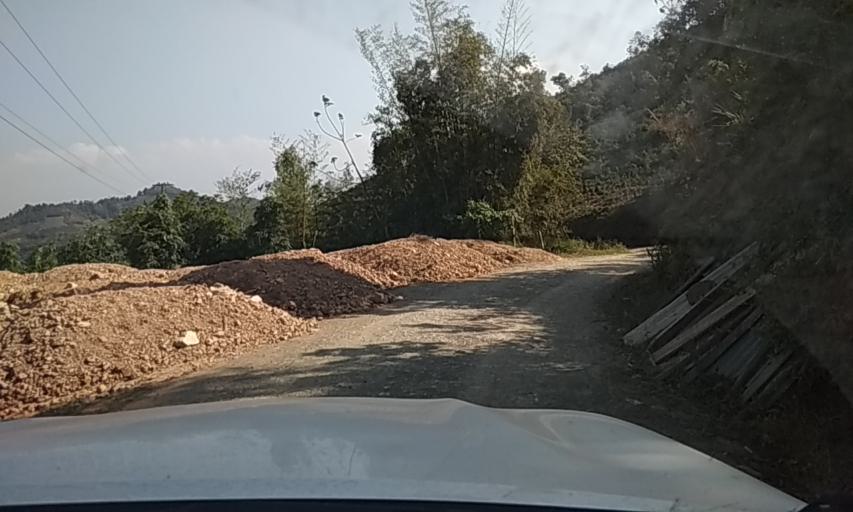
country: LA
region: Phongsali
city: Phongsali
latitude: 21.6533
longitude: 102.0916
